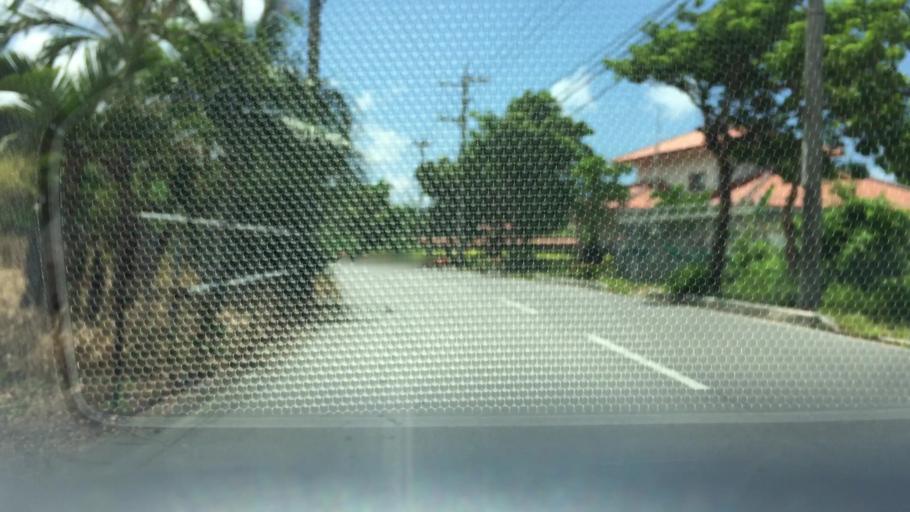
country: JP
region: Okinawa
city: Ishigaki
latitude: 24.3625
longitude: 124.1170
